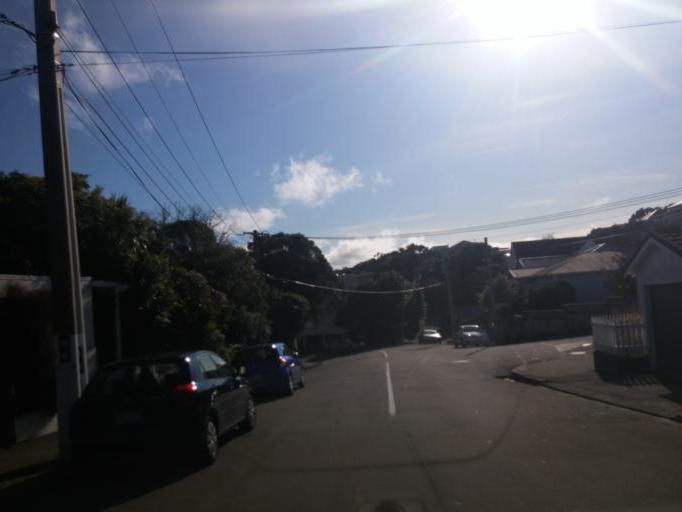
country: NZ
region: Wellington
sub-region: Wellington City
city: Brooklyn
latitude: -41.3072
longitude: 174.7643
